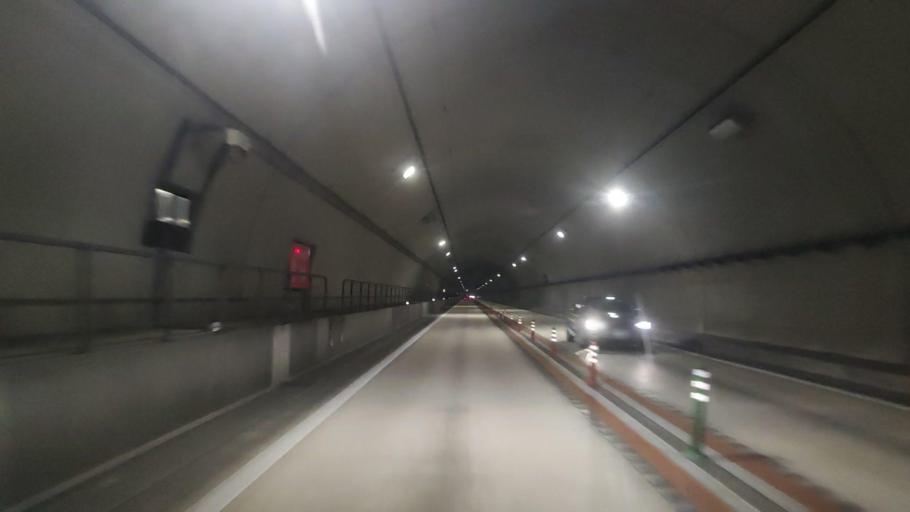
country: JP
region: Wakayama
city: Tanabe
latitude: 33.5670
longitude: 135.4916
